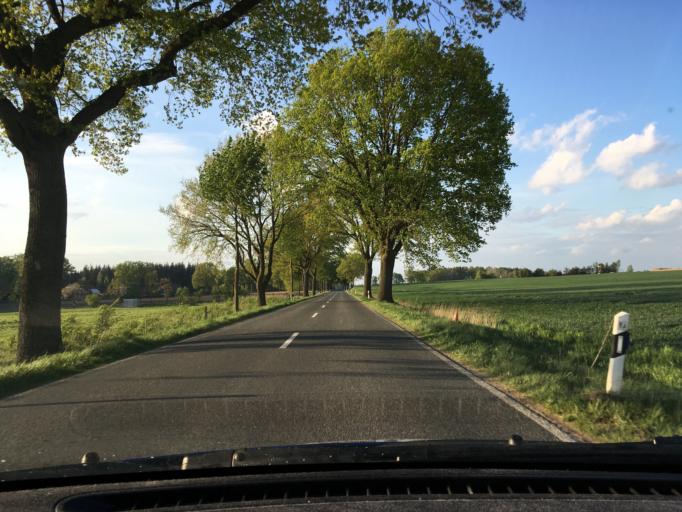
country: DE
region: Lower Saxony
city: Wietzendorf
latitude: 52.8879
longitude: 9.9832
